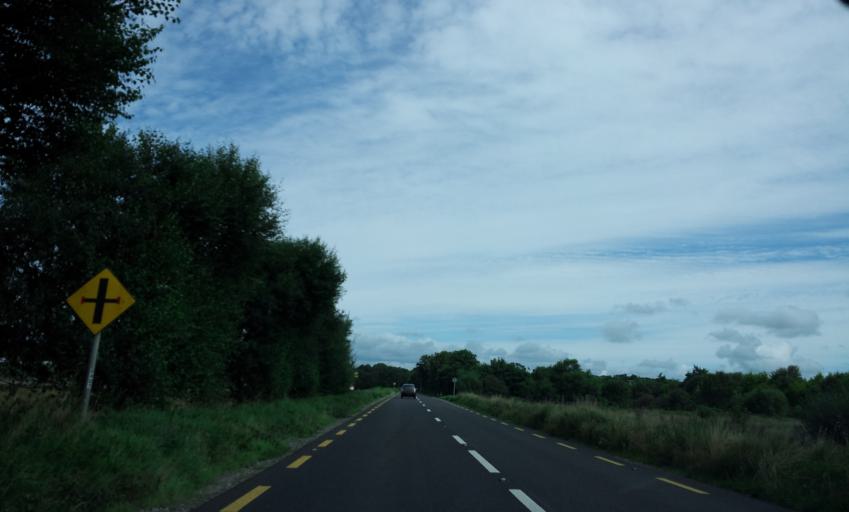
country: IE
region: Munster
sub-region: Ciarrai
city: Killorglin
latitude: 52.0962
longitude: -9.8341
